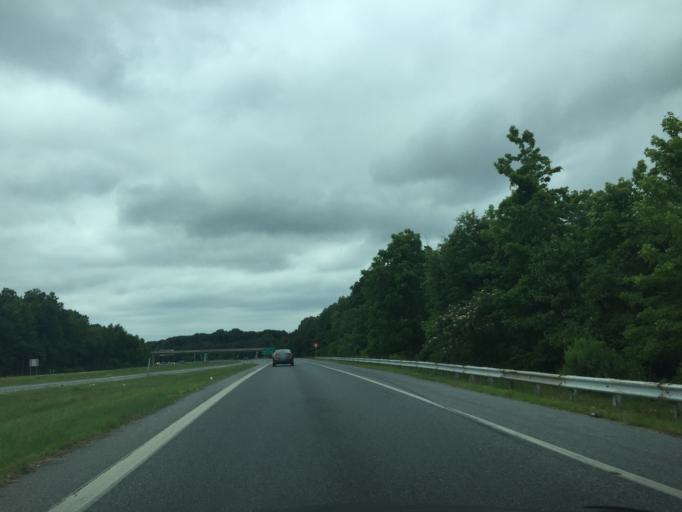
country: US
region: Maryland
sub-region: Baltimore County
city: Essex
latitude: 39.3202
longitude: -76.4586
